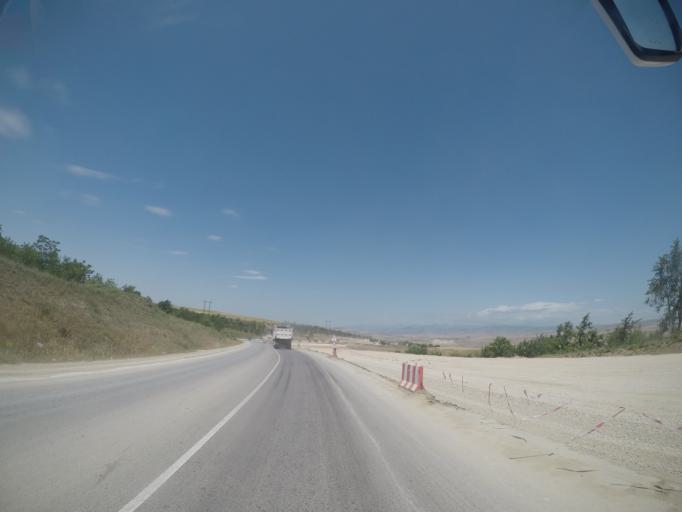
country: AZ
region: Qobustan
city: Qobustan
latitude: 40.5334
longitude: 48.7812
